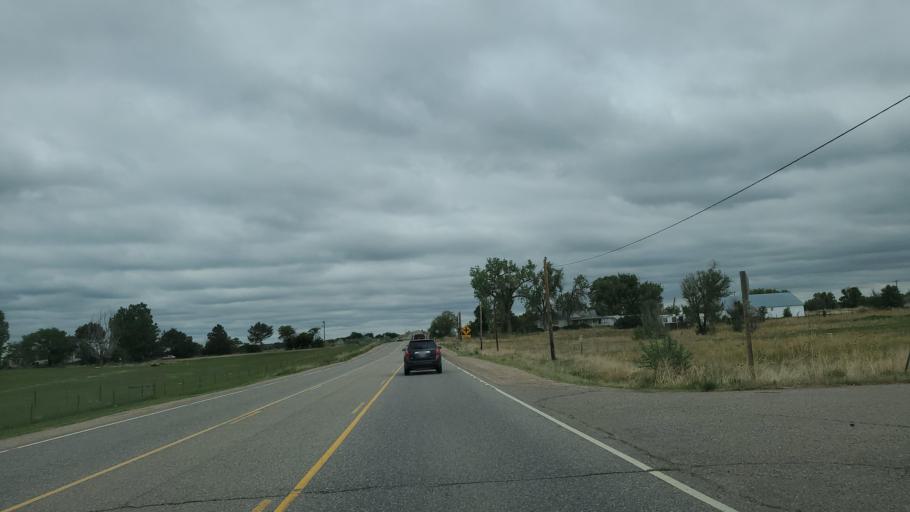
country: US
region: Colorado
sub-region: Adams County
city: Brighton
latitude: 39.9143
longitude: -104.8311
